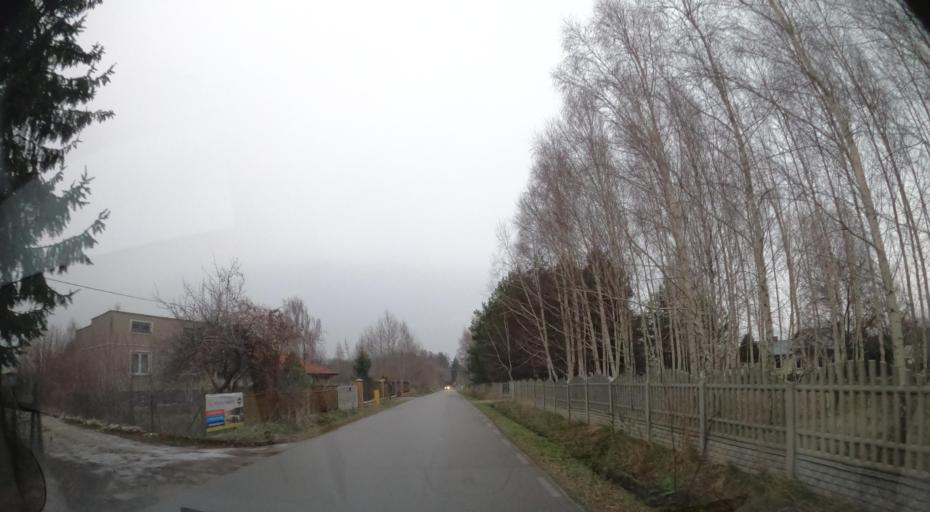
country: PL
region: Masovian Voivodeship
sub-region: Powiat radomski
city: Jastrzebia
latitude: 51.4212
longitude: 21.2258
